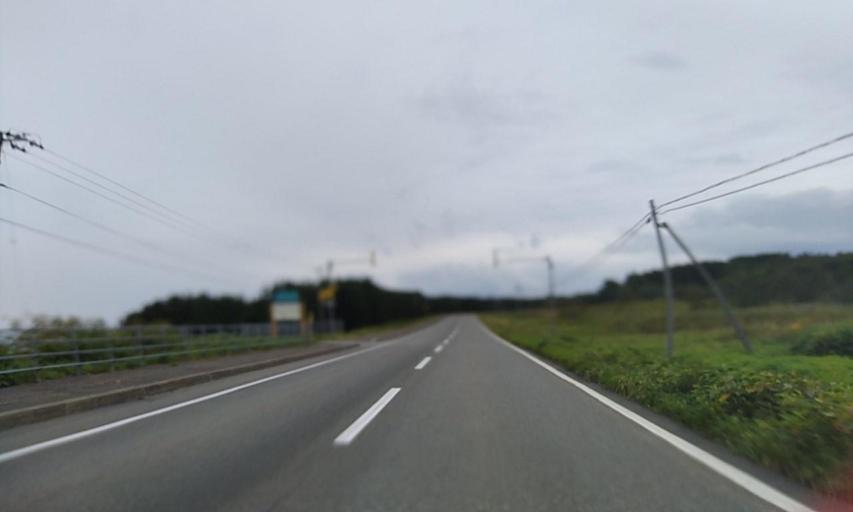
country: JP
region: Hokkaido
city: Nayoro
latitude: 45.0284
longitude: 142.5238
